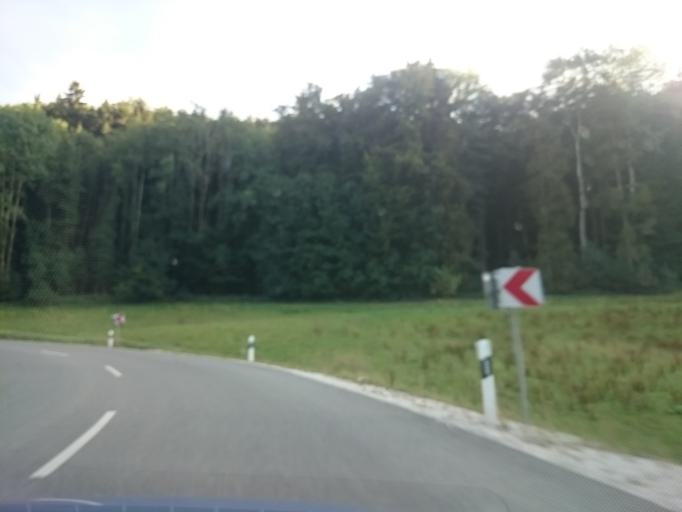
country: DE
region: Bavaria
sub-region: Regierungsbezirk Mittelfranken
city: Thalmassing
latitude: 49.0781
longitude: 11.1959
